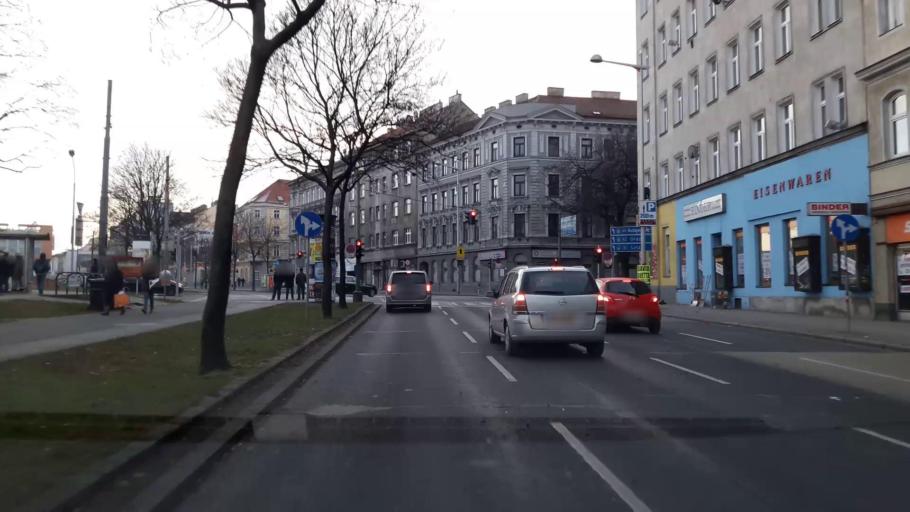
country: AT
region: Vienna
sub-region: Wien Stadt
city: Vienna
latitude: 48.2065
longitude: 16.3368
